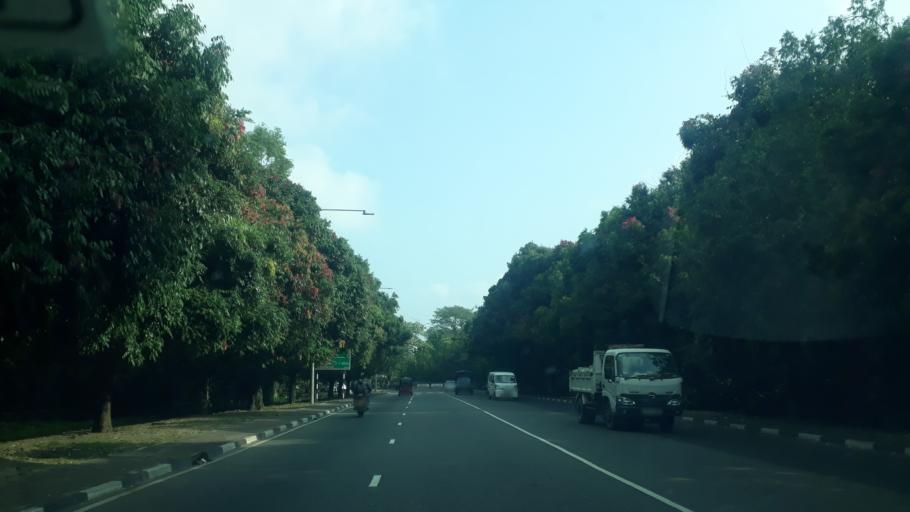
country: LK
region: Western
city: Battaramulla South
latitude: 6.8950
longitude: 79.9153
